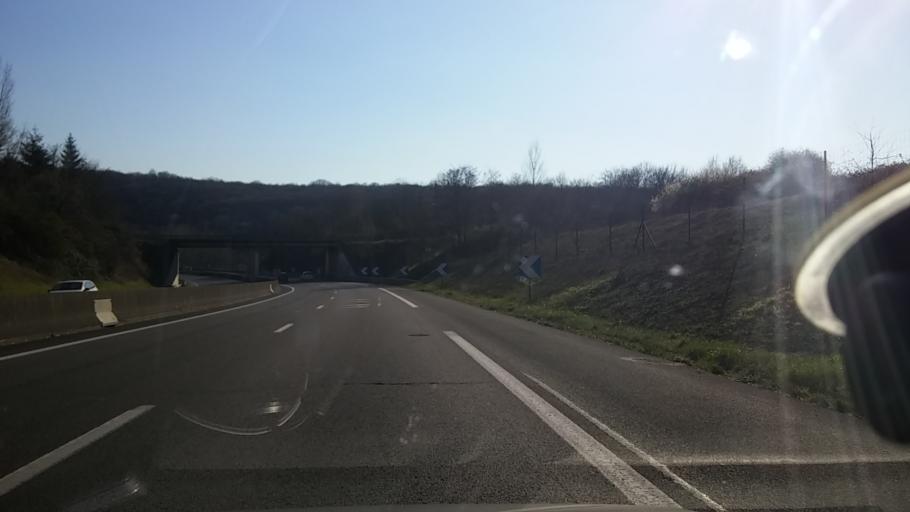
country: FR
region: Centre
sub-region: Departement de l'Indre
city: Saint-Marcel
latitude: 46.6045
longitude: 1.5007
